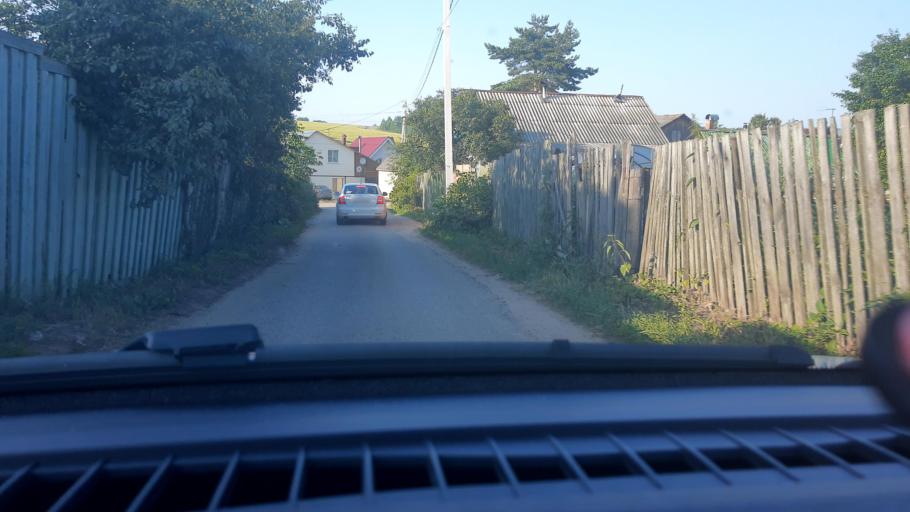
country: RU
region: Nizjnij Novgorod
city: Nizhniy Novgorod
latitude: 56.1965
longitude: 43.9584
